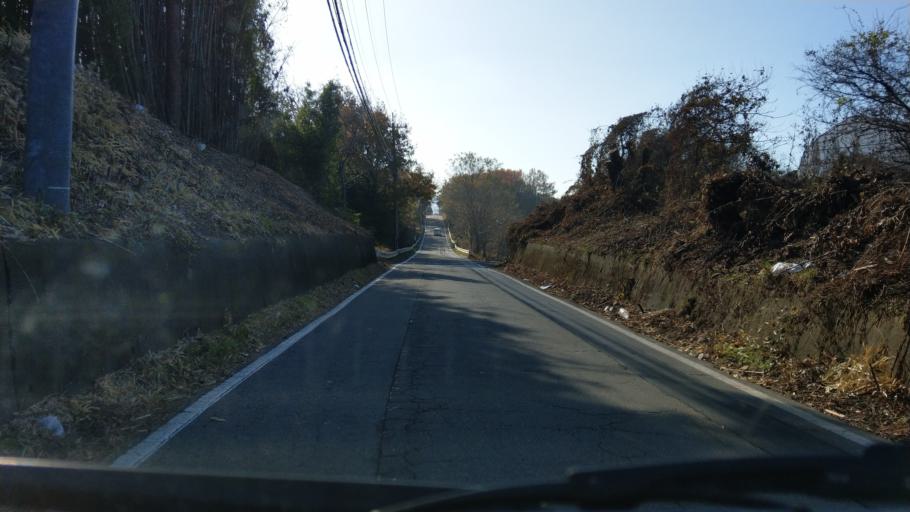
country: JP
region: Nagano
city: Komoro
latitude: 36.2968
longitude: 138.4856
